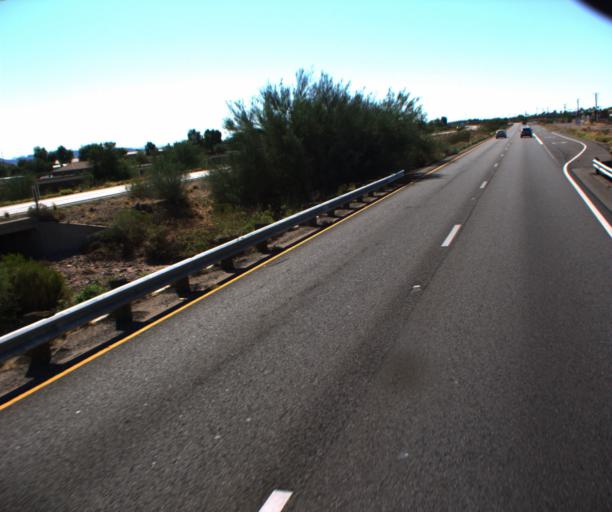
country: US
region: Arizona
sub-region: Pinal County
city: Apache Junction
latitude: 33.3648
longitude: -111.4763
